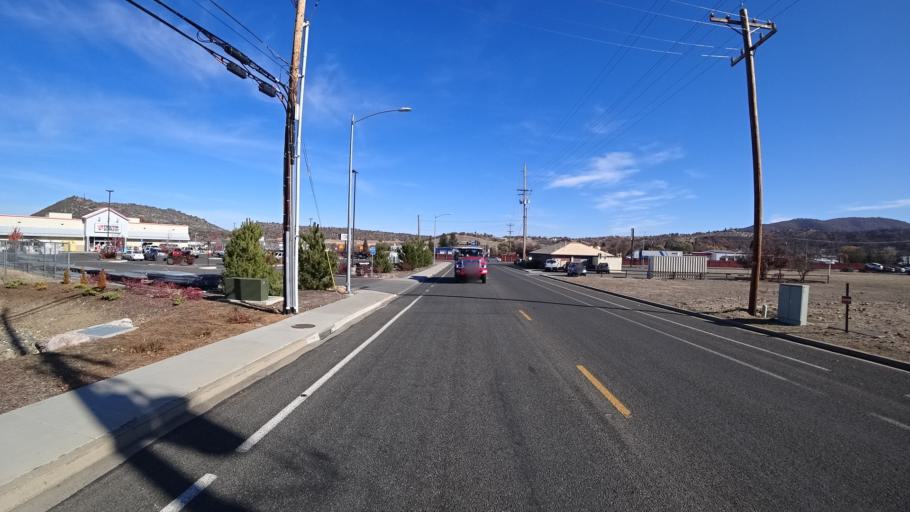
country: US
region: California
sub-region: Siskiyou County
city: Yreka
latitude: 41.7120
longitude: -122.6429
